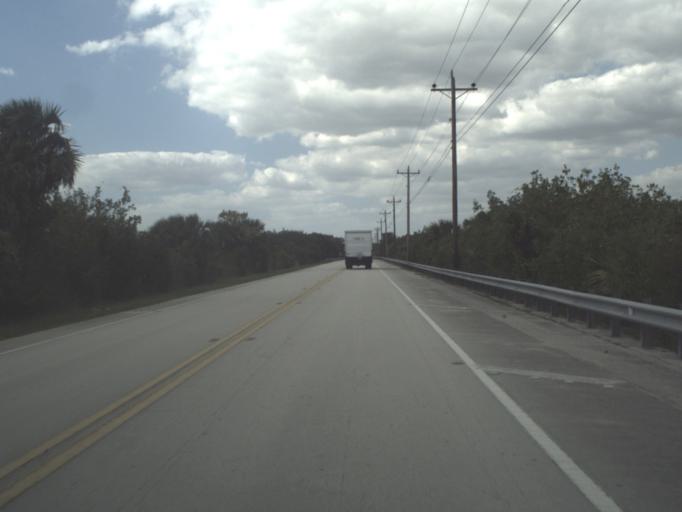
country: US
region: Florida
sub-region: Collier County
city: Marco
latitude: 25.9795
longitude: -81.5601
